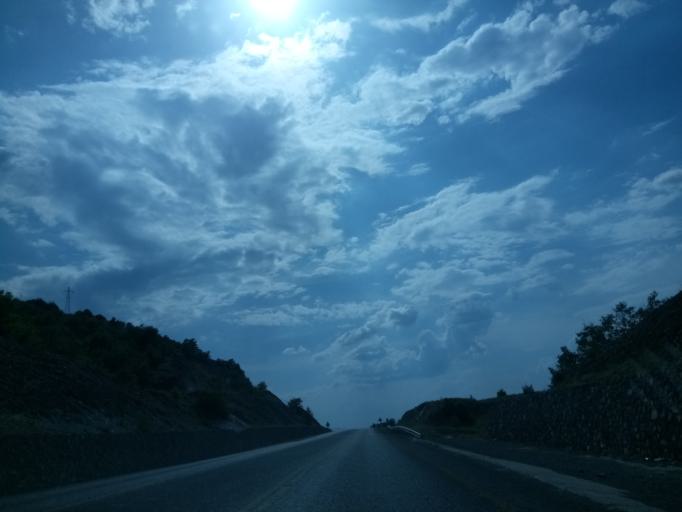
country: TR
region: Isparta
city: Bagkonak
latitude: 38.2257
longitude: 31.3017
